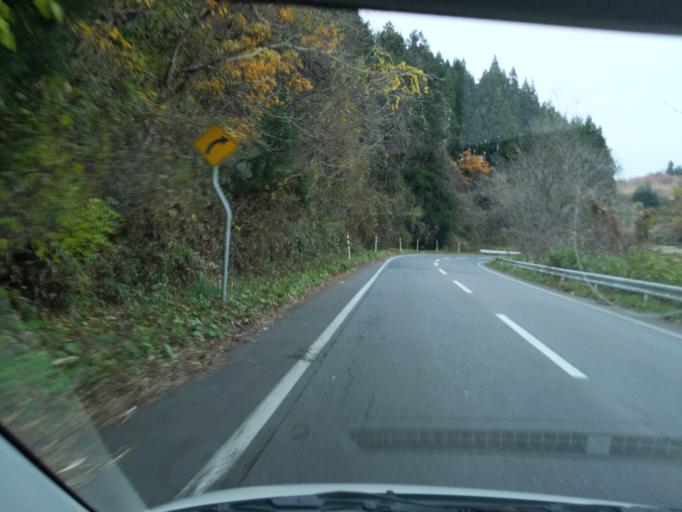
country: JP
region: Iwate
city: Kitakami
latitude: 39.2277
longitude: 141.2781
